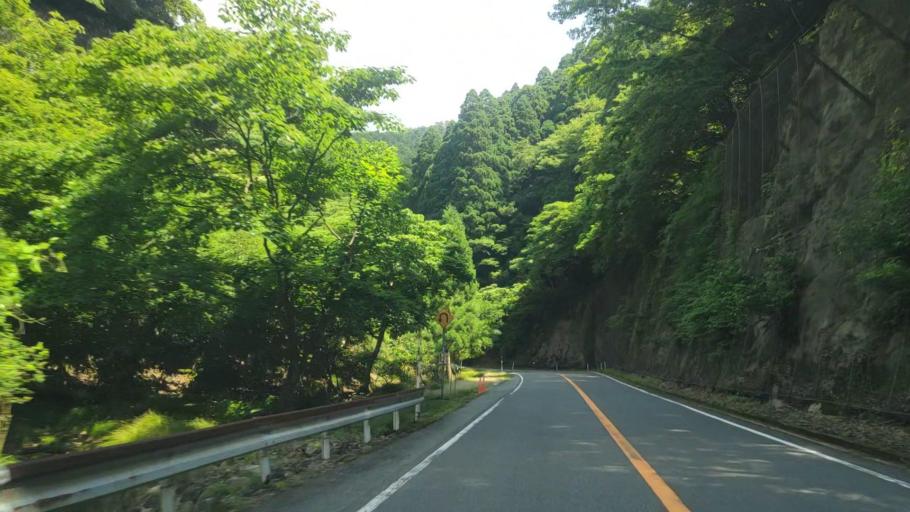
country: JP
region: Hyogo
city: Toyooka
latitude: 35.6367
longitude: 134.7801
